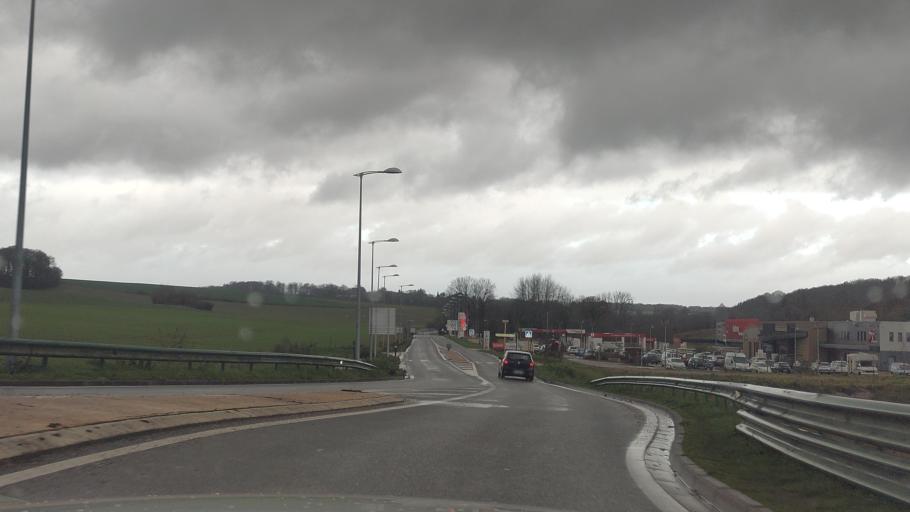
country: FR
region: Picardie
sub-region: Departement de l'Oise
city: Saint-Omer-en-Chaussee
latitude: 49.5794
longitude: 1.9537
